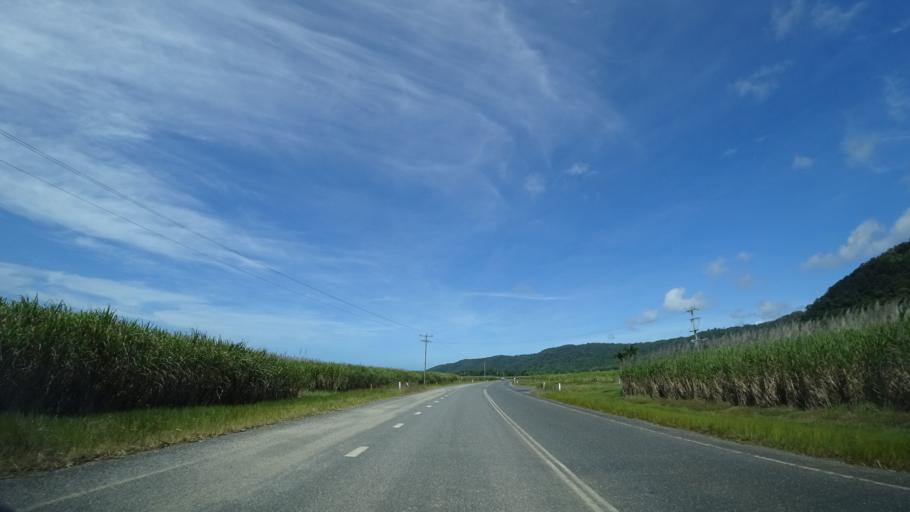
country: AU
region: Queensland
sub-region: Cairns
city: Port Douglas
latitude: -16.2932
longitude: 145.3881
